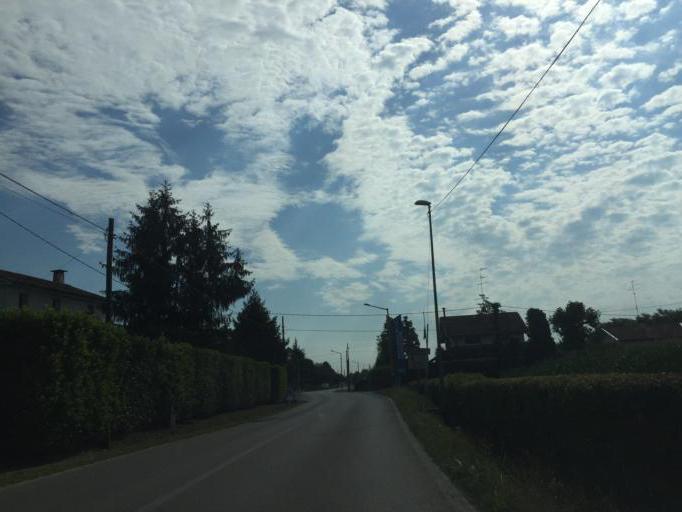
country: IT
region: Veneto
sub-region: Provincia di Treviso
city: Cordignano
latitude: 45.9570
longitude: 12.4241
